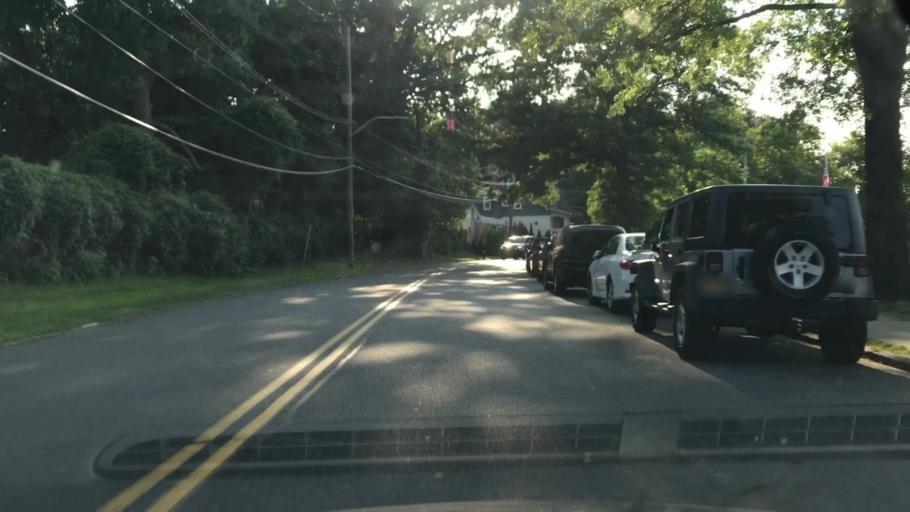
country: US
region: New York
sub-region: Westchester County
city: Yonkers
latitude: 40.9429
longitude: -73.8723
